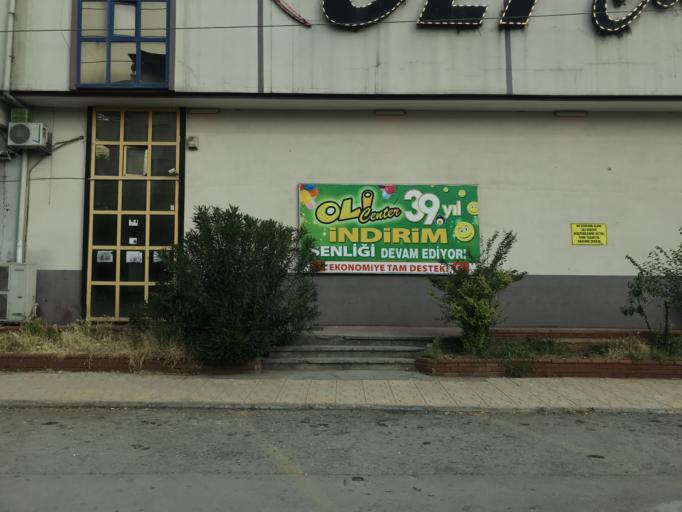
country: TR
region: Gaziantep
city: Sahinbey
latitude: 37.0532
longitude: 37.3367
